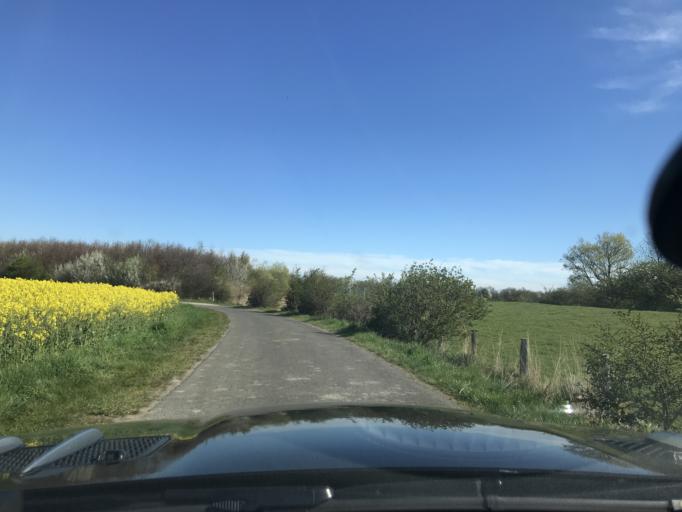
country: DE
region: Schleswig-Holstein
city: Grossenbrode
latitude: 54.4623
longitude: 11.0226
